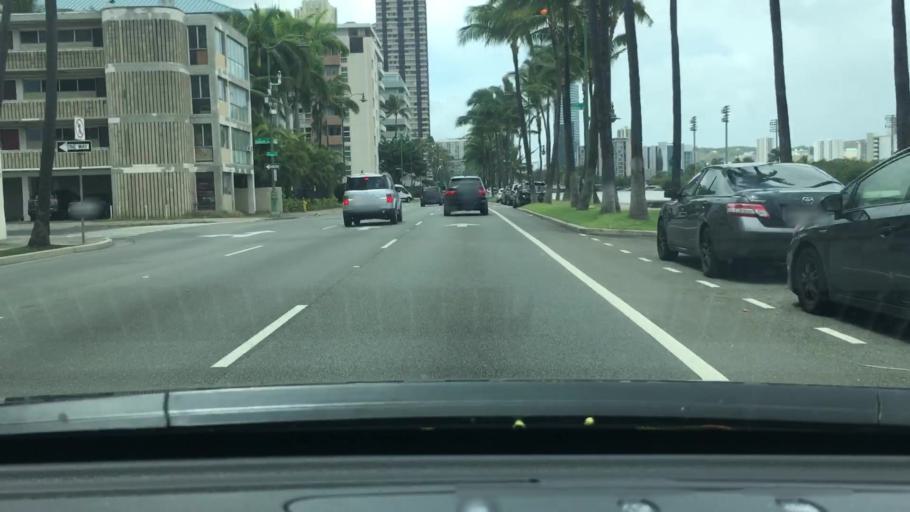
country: US
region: Hawaii
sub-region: Honolulu County
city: Honolulu
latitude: 21.2846
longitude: -157.8292
